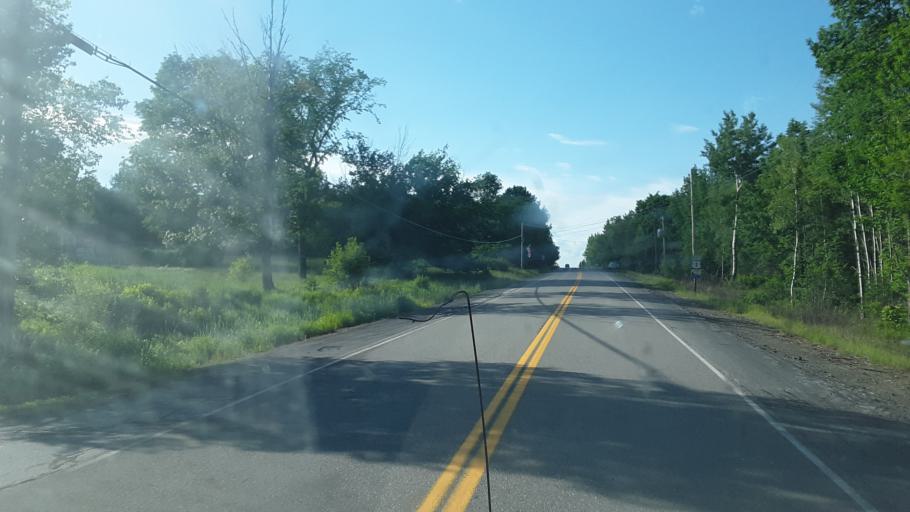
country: US
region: Maine
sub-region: Washington County
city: Calais
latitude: 45.3260
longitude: -67.6894
